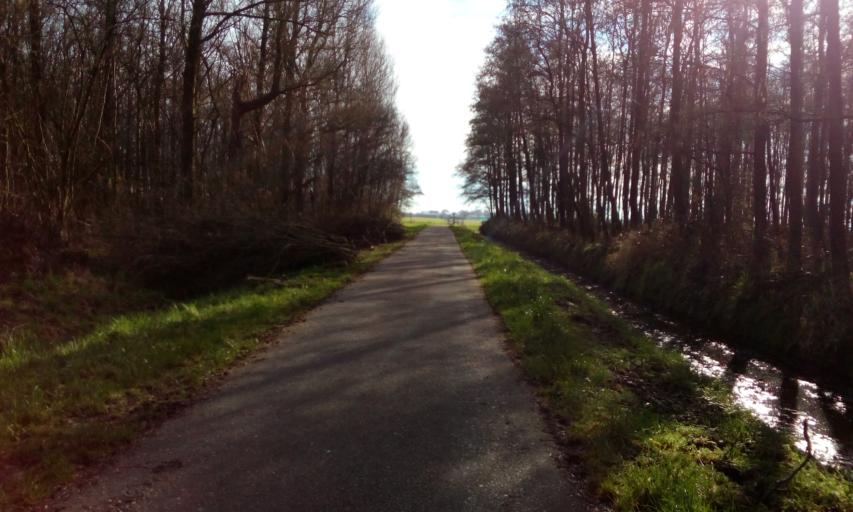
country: NL
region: South Holland
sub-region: Gemeente Alphen aan den Rijn
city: Alphen aan den Rijn
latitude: 52.1136
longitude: 4.6039
